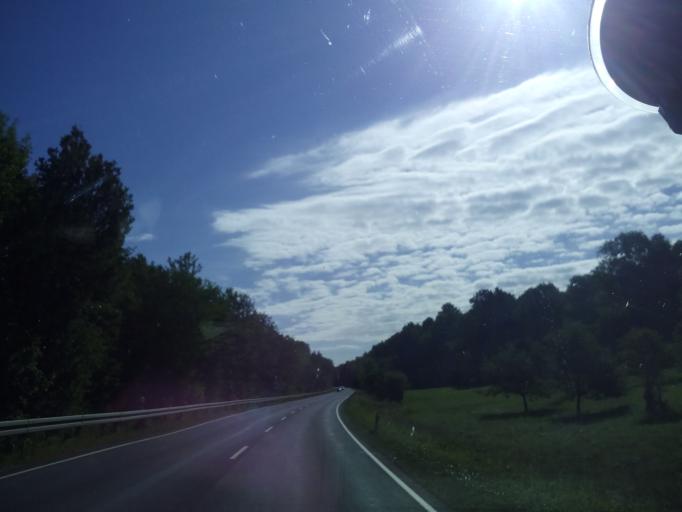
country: DE
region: Bavaria
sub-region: Upper Franconia
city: Buttenheim
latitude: 49.8052
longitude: 11.0513
